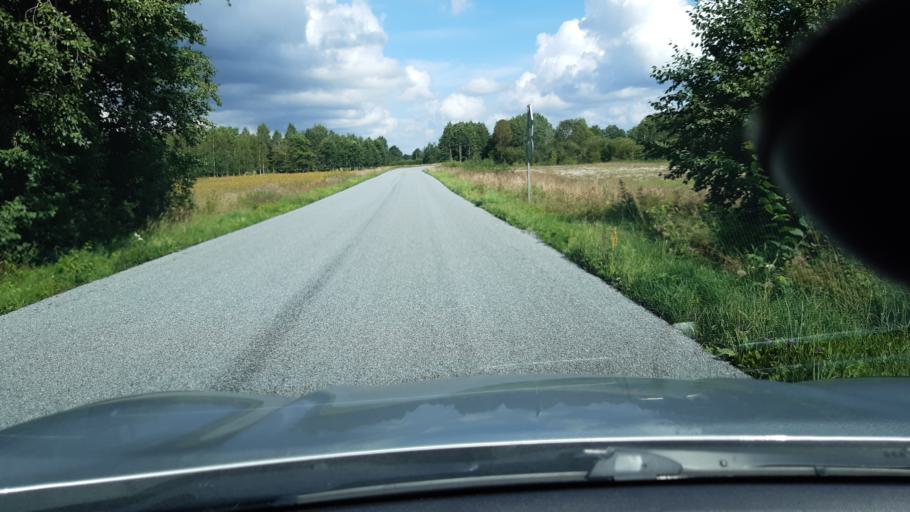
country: EE
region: Raplamaa
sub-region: Kehtna vald
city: Kehtna
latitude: 58.9070
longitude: 25.1023
